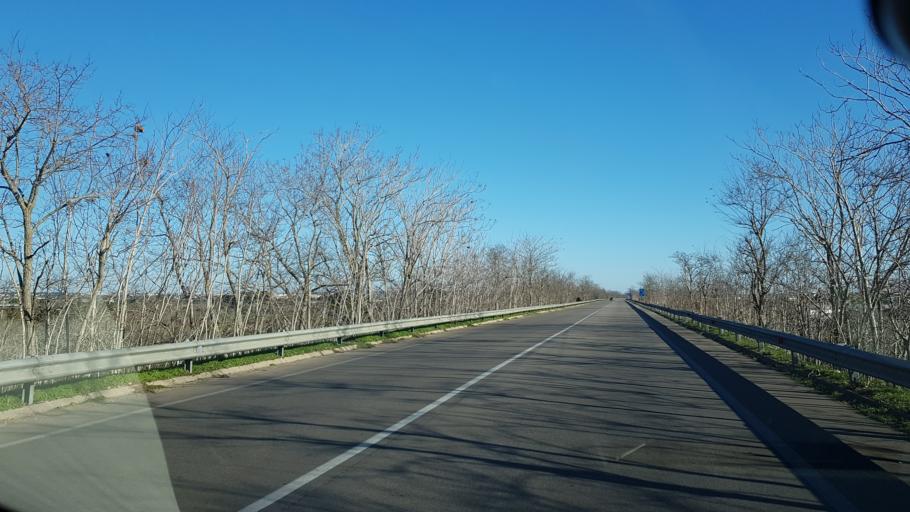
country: IT
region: Apulia
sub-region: Provincia di Lecce
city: Taviano
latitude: 39.9962
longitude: 18.0889
